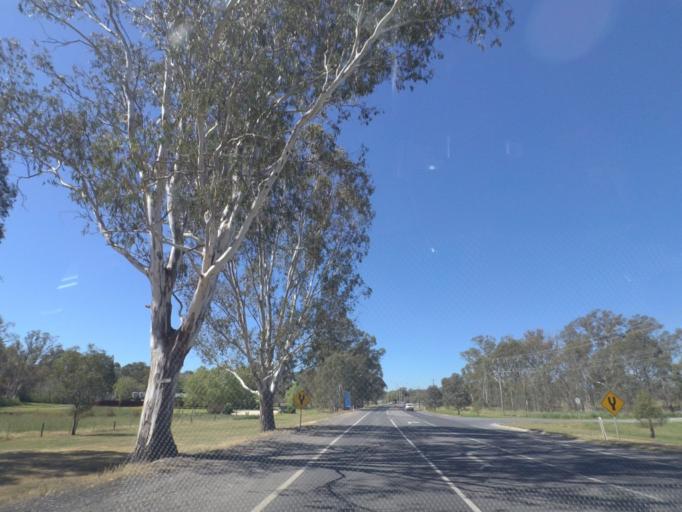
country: AU
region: Victoria
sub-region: Murrindindi
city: Kinglake West
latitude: -37.0238
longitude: 145.1136
